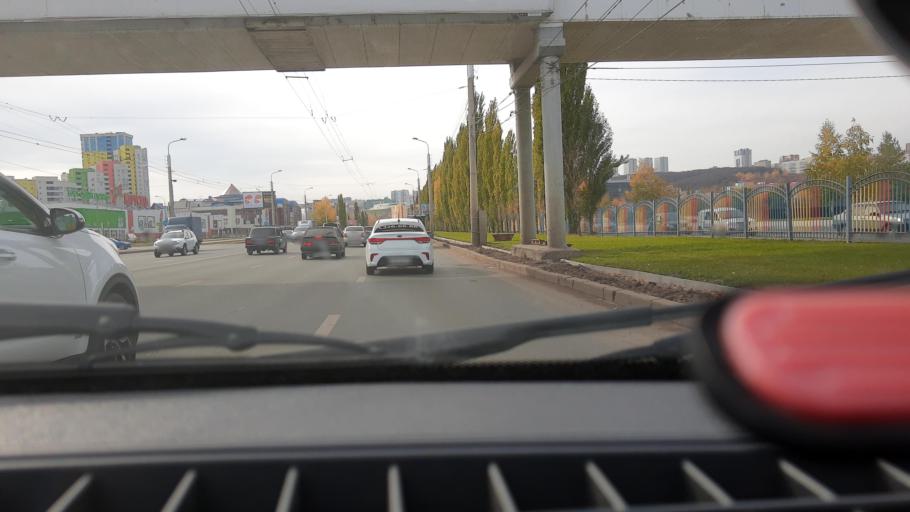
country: RU
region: Bashkortostan
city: Ufa
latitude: 54.7734
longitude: 56.0631
